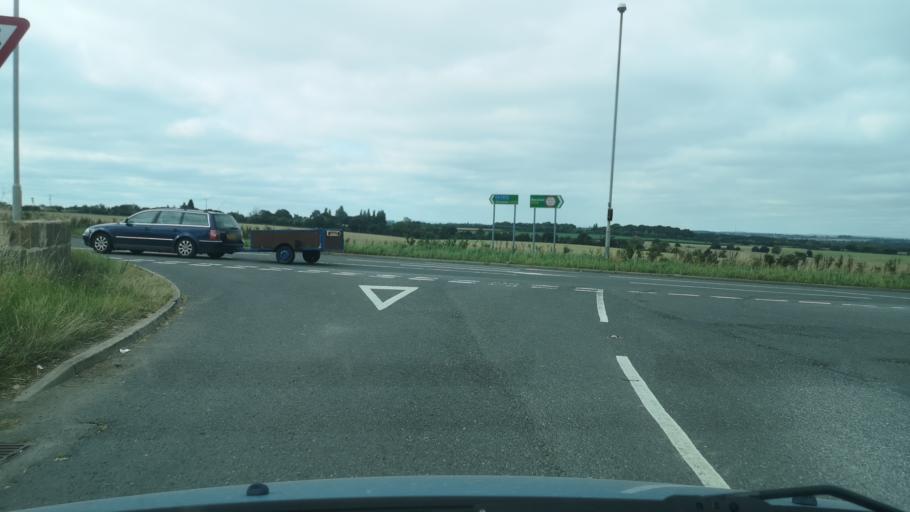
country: GB
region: England
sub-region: City and Borough of Wakefield
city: Badsworth
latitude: 53.6254
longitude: -1.3144
